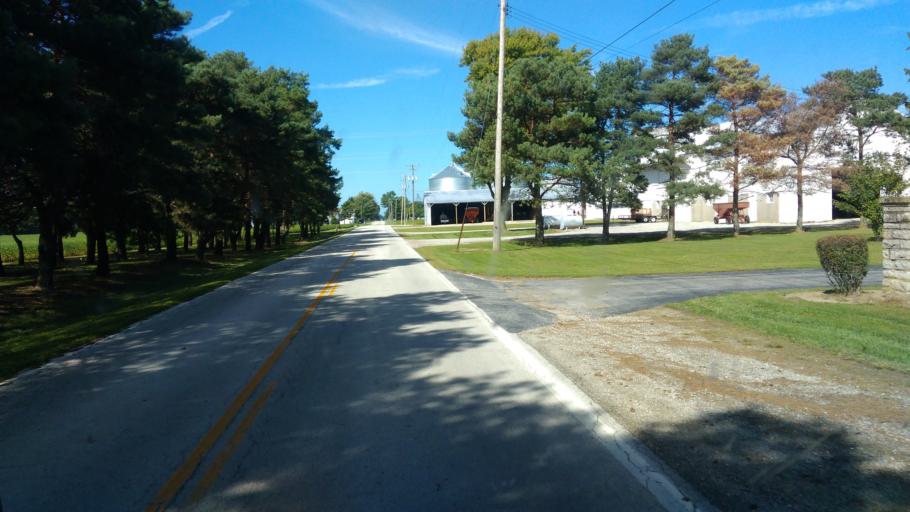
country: US
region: Ohio
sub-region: Sandusky County
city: Clyde
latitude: 41.3872
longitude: -82.8922
